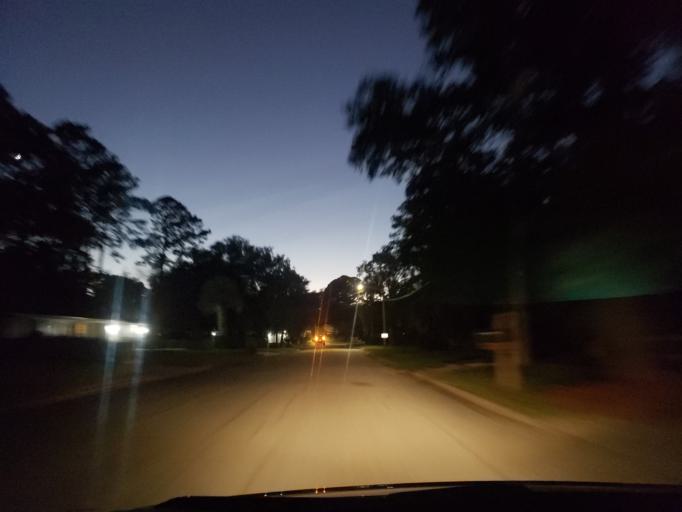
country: US
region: Georgia
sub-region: Chatham County
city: Isle of Hope
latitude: 31.9861
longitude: -81.0598
